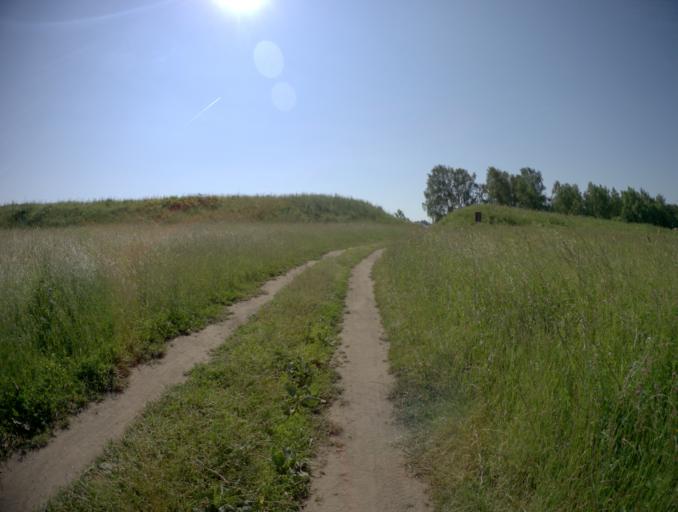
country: RU
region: Vladimir
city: Novovyazniki
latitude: 56.2358
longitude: 42.2451
